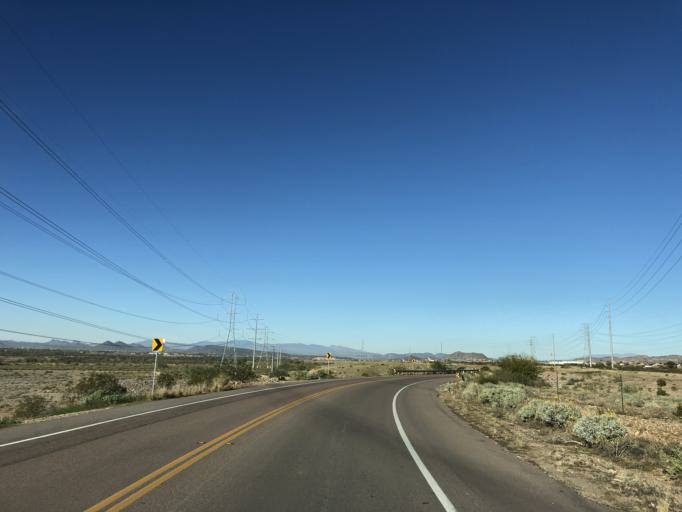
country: US
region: Arizona
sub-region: Maricopa County
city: Sun City West
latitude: 33.6778
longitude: -112.2999
